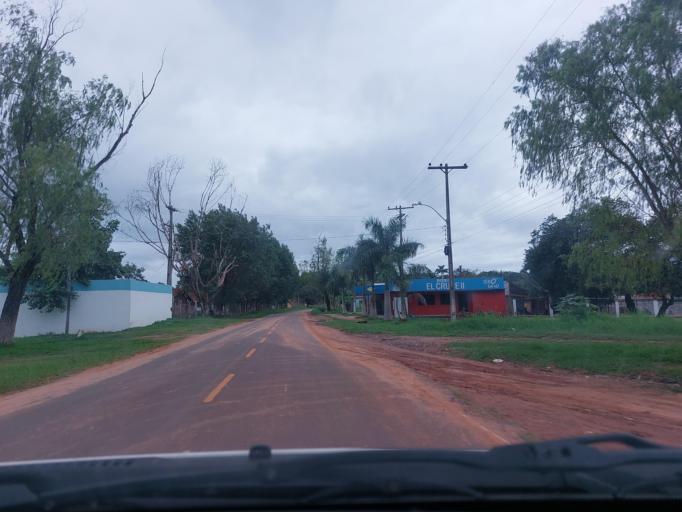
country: PY
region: San Pedro
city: Guayaybi
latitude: -24.6552
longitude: -56.4374
